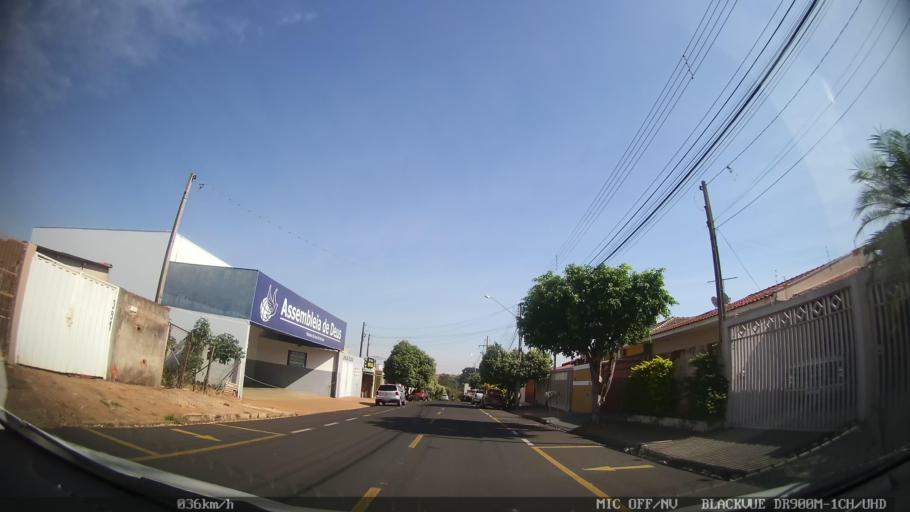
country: BR
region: Sao Paulo
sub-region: Sao Jose Do Rio Preto
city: Sao Jose do Rio Preto
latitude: -20.7878
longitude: -49.4331
